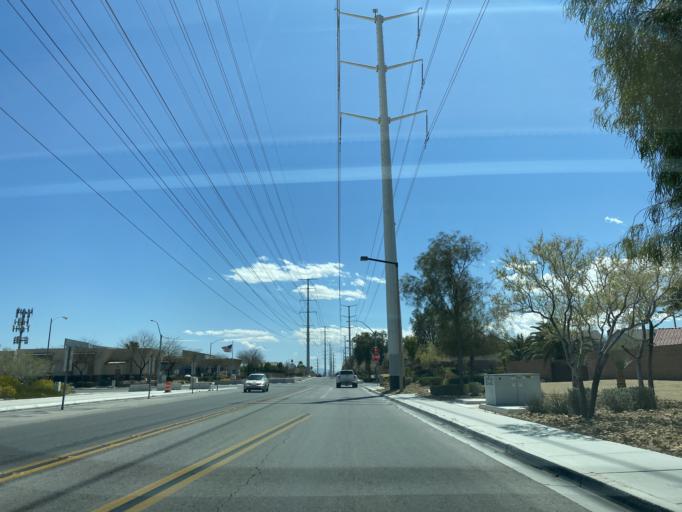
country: US
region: Nevada
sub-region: Clark County
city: North Las Vegas
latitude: 36.3142
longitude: -115.2072
